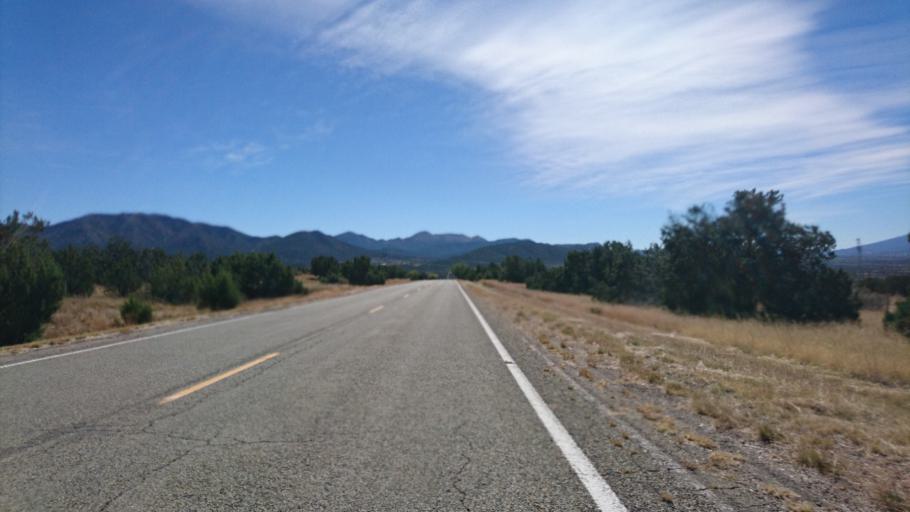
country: US
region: New Mexico
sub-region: Bernalillo County
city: Sandia Knolls
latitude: 35.2971
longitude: -106.2159
